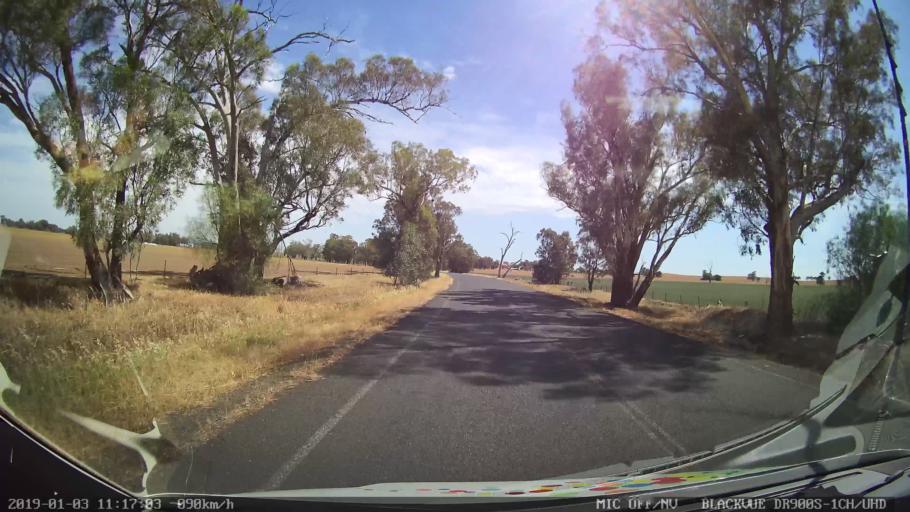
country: AU
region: New South Wales
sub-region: Young
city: Young
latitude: -34.1436
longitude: 148.2676
